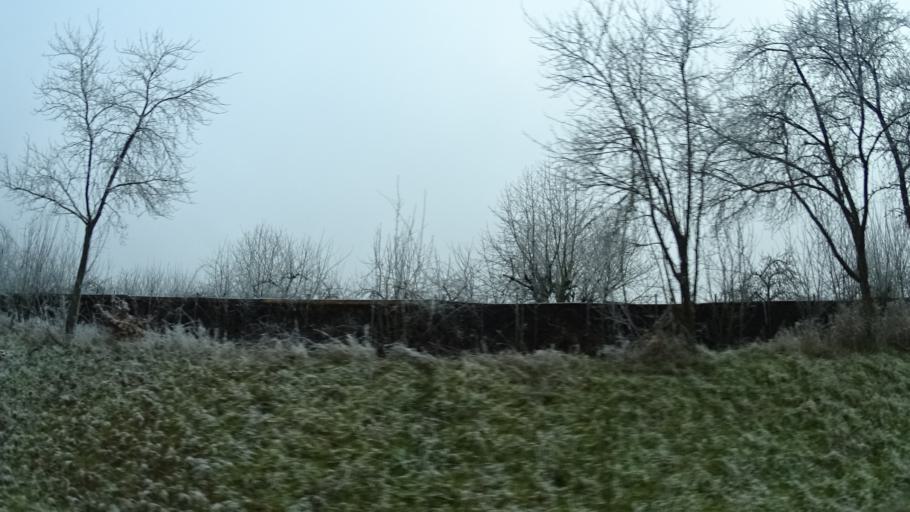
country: DE
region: Baden-Wuerttemberg
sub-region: Karlsruhe Region
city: Rosenberg
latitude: 49.4532
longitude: 9.4720
